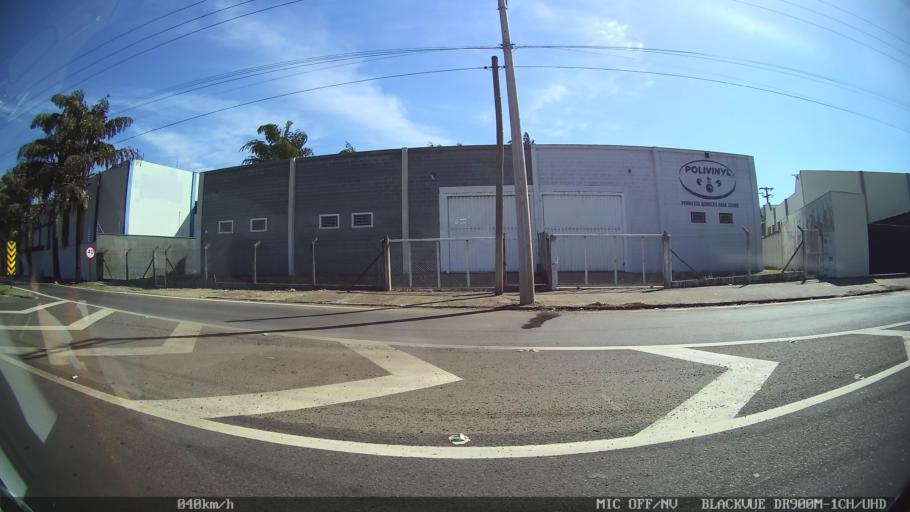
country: BR
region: Sao Paulo
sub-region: Franca
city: Franca
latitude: -20.5560
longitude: -47.4400
